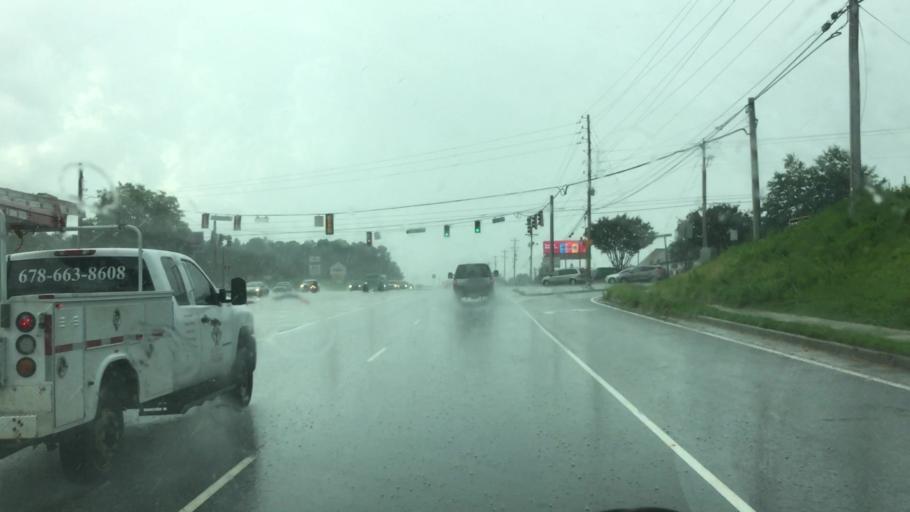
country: US
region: Georgia
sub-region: Forsyth County
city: Cumming
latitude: 34.1730
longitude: -84.1263
